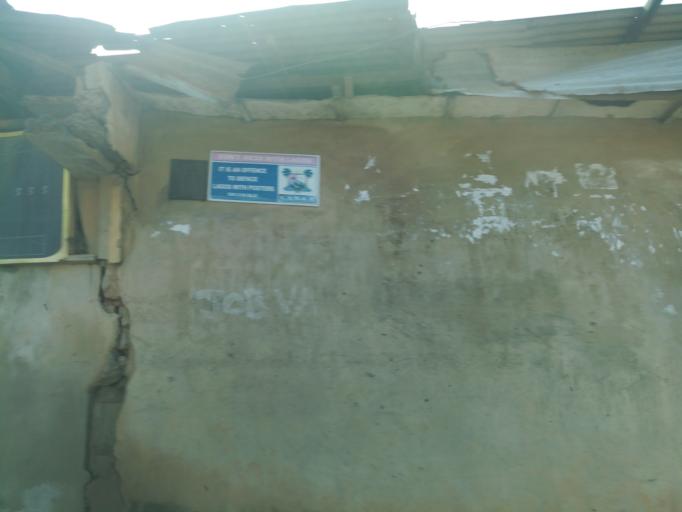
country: NG
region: Lagos
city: Ebute Ikorodu
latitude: 6.6244
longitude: 3.4819
